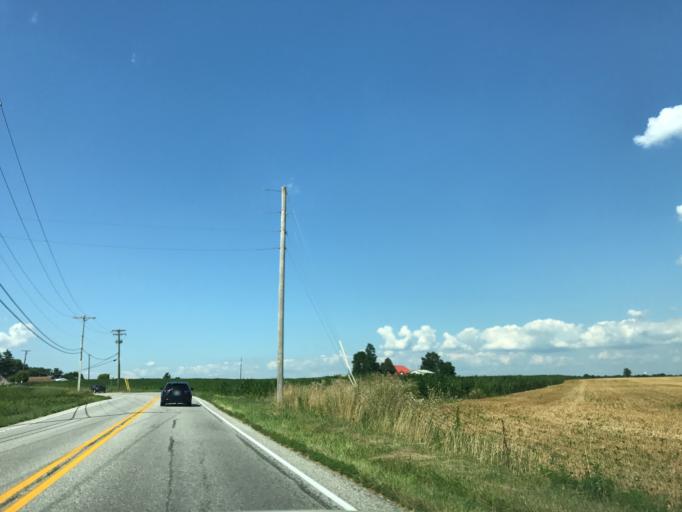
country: US
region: Pennsylvania
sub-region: Adams County
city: McSherrystown
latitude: 39.7922
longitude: -77.0415
